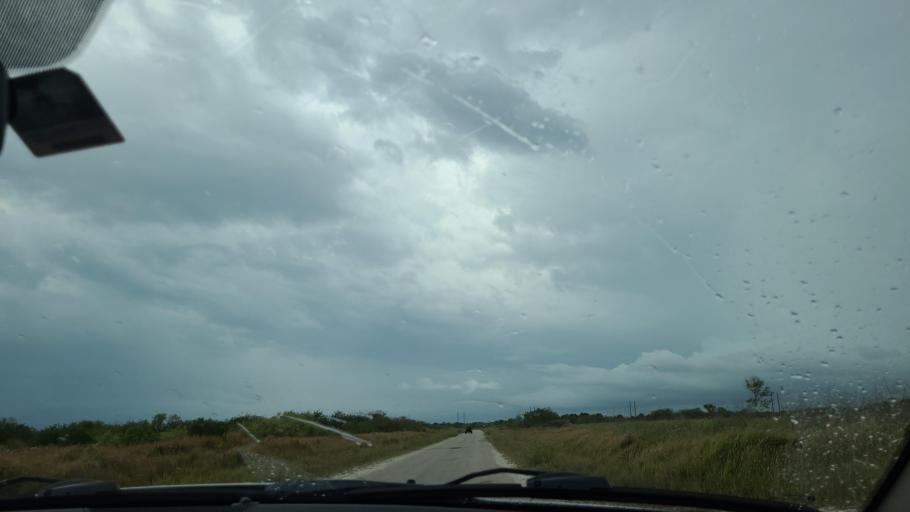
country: US
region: Florida
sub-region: Brevard County
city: June Park
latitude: 27.9517
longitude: -80.7065
